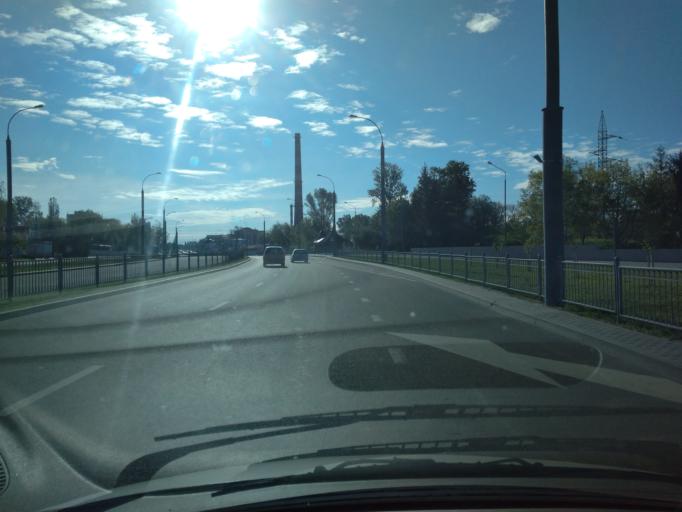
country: BY
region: Brest
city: Brest
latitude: 52.0854
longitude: 23.6707
